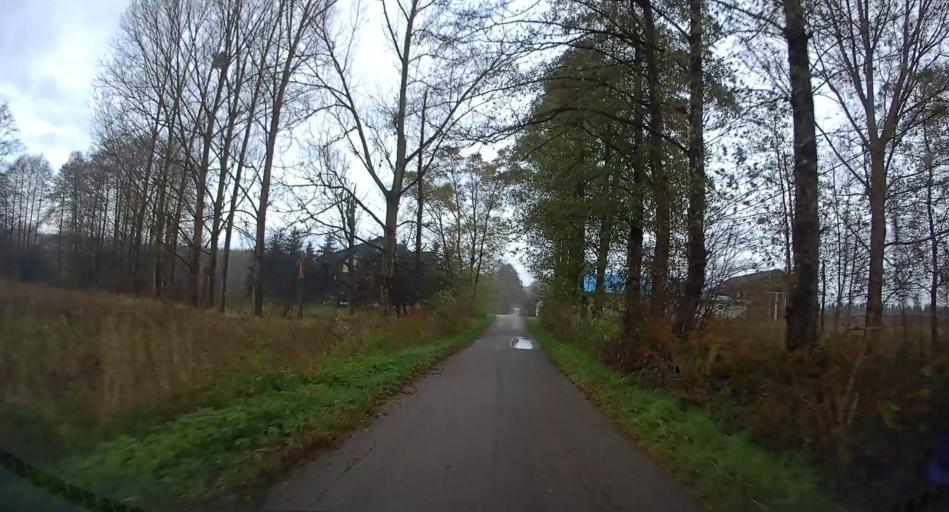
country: PL
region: Lodz Voivodeship
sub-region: Powiat skierniewicki
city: Kowiesy
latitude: 51.9337
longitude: 20.4028
